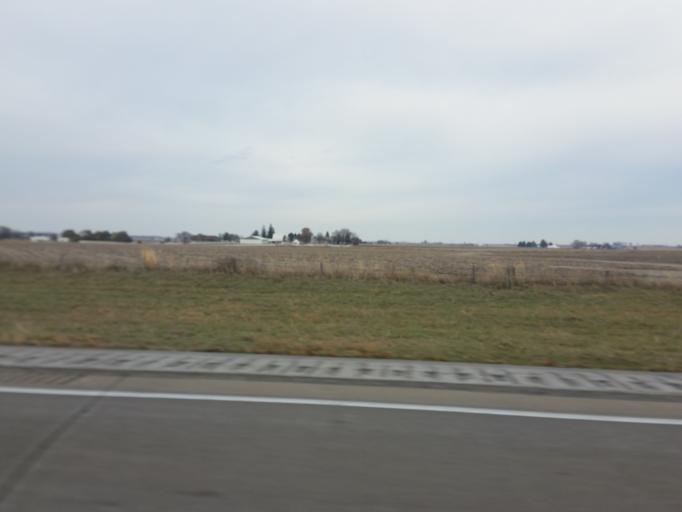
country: US
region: Iowa
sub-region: Scott County
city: Walcott
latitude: 41.6039
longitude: -90.6995
